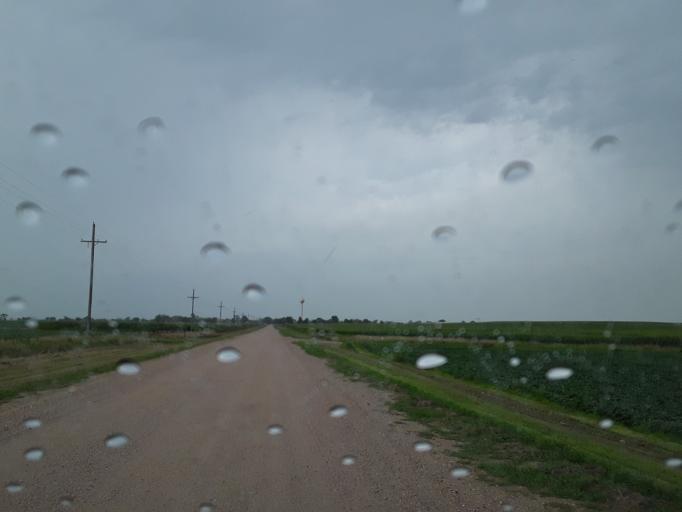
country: US
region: Nebraska
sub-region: Saunders County
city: Yutan
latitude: 41.1748
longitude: -96.4448
